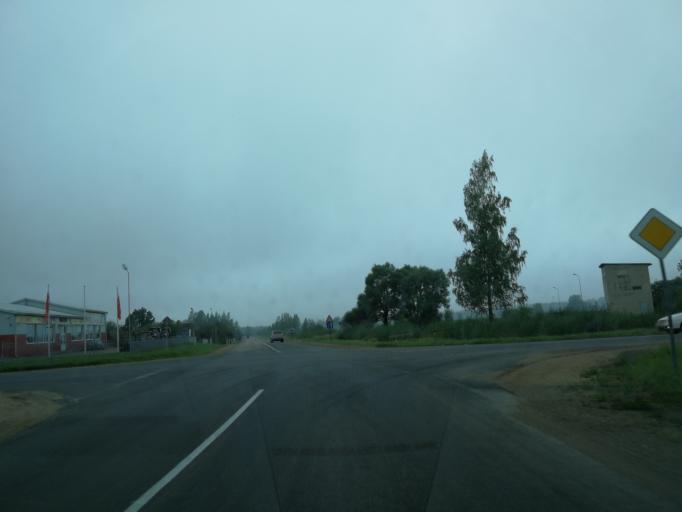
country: LV
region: Preilu Rajons
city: Preili
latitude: 56.2995
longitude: 26.7310
